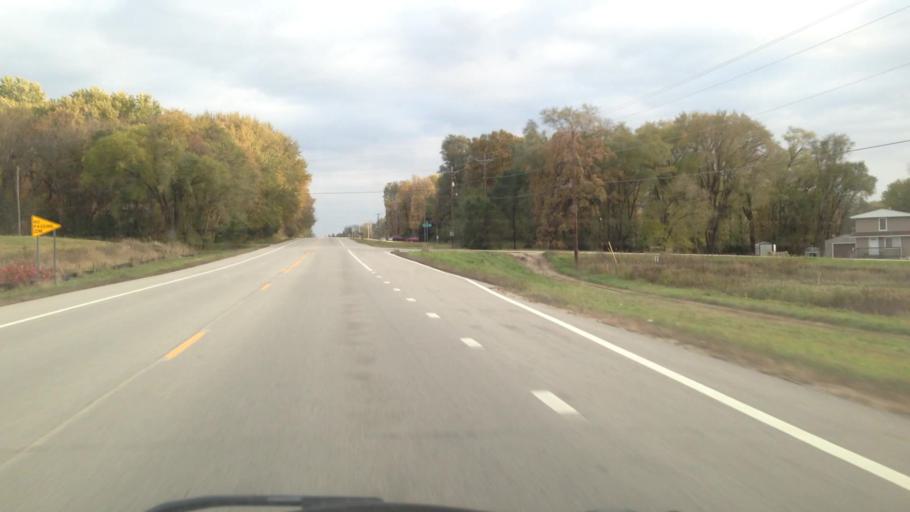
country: US
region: Minnesota
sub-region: Olmsted County
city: Rochester
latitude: 43.9790
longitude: -92.3976
